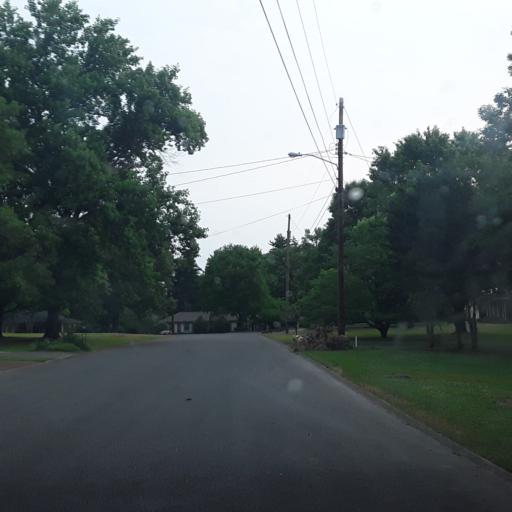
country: US
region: Tennessee
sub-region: Williamson County
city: Brentwood
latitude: 36.0553
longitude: -86.7614
